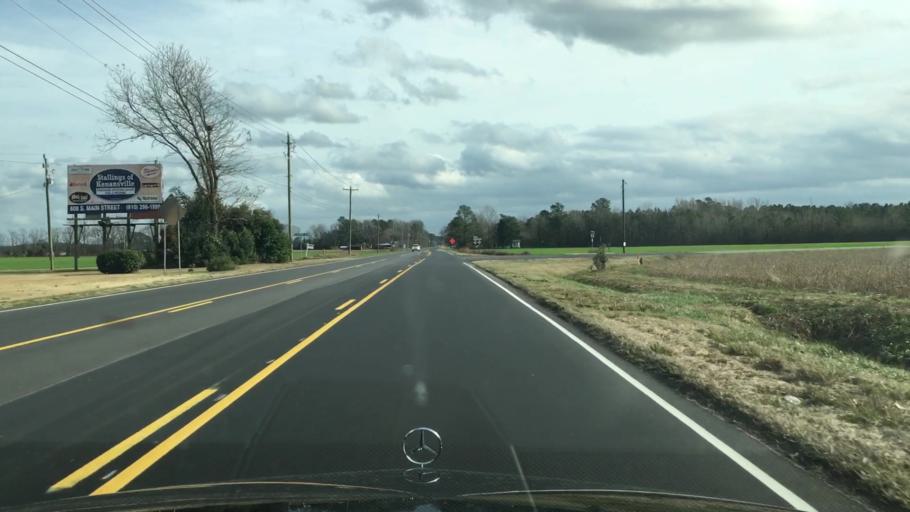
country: US
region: North Carolina
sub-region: Duplin County
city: Warsaw
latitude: 34.9841
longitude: -78.0401
